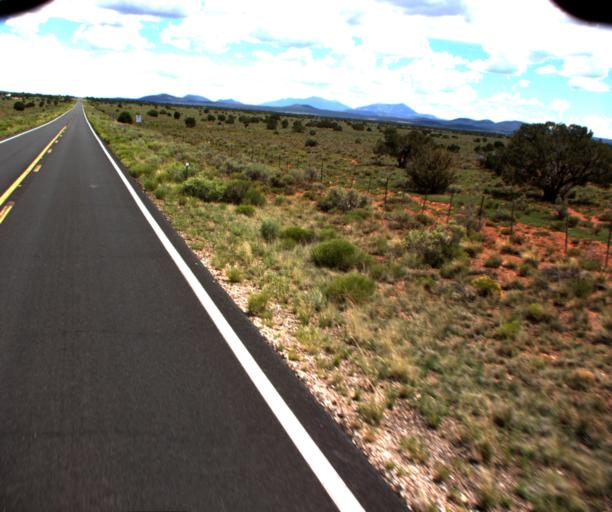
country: US
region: Arizona
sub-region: Coconino County
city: Williams
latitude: 35.6180
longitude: -112.0917
